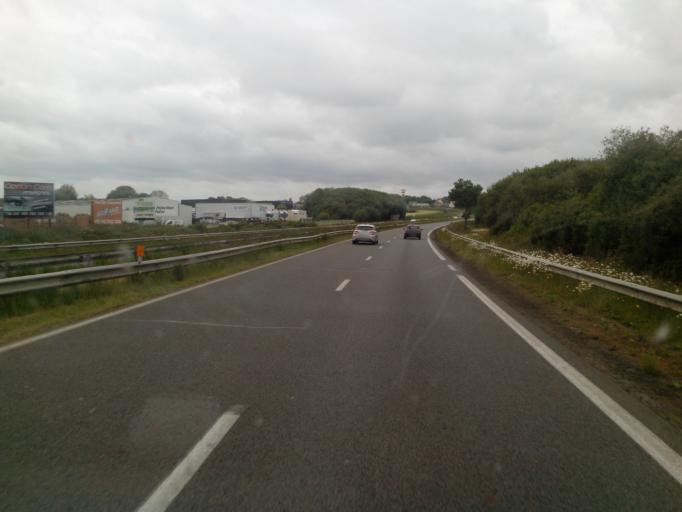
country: FR
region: Brittany
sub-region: Departement des Cotes-d'Armor
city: Tremuson
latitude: 48.5254
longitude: -2.8666
